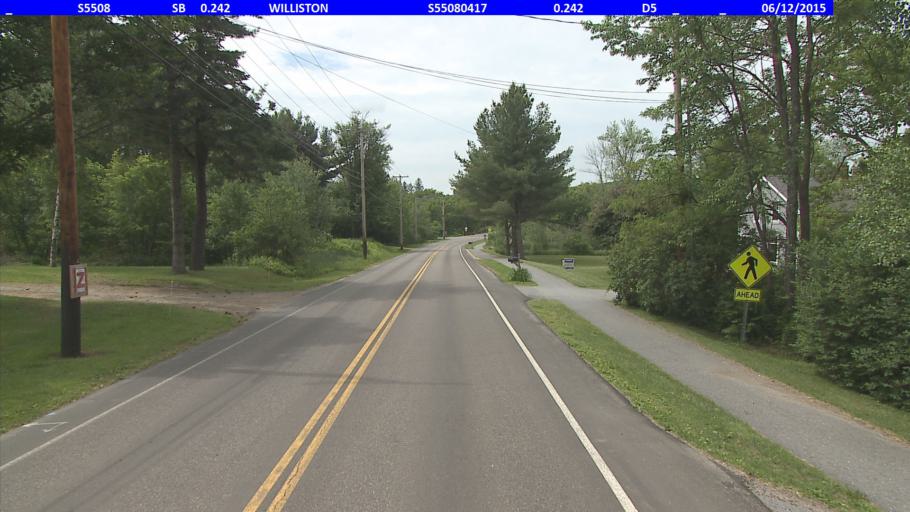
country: US
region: Vermont
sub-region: Chittenden County
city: Williston
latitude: 44.4404
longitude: -73.0657
